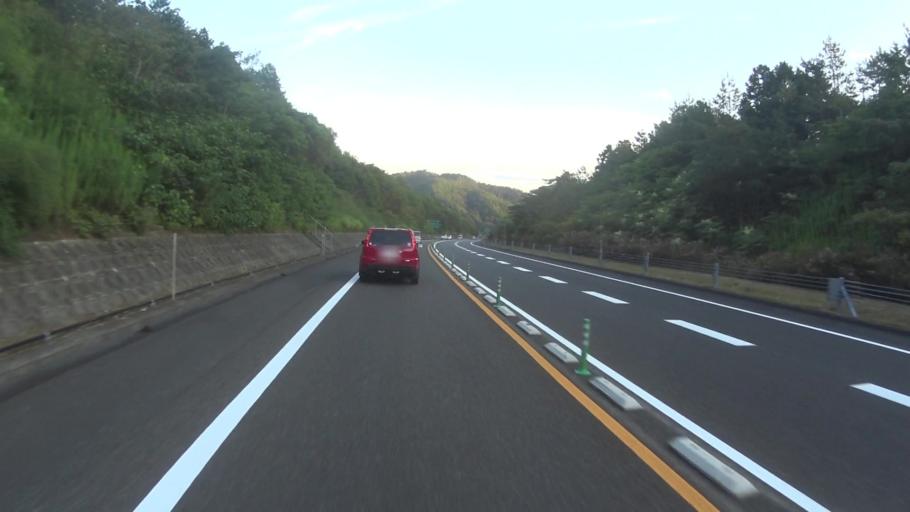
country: JP
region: Kyoto
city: Ayabe
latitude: 35.3922
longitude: 135.2391
